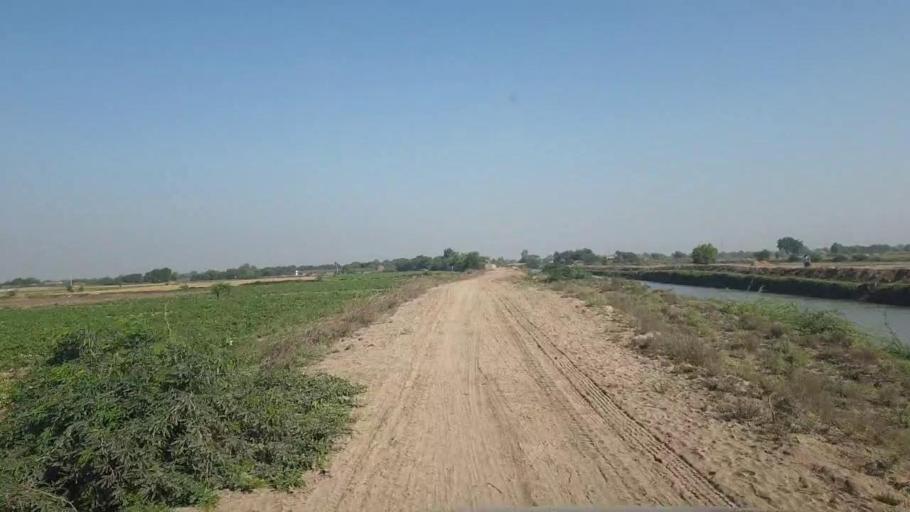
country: PK
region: Sindh
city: Badin
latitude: 24.7267
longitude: 68.8040
